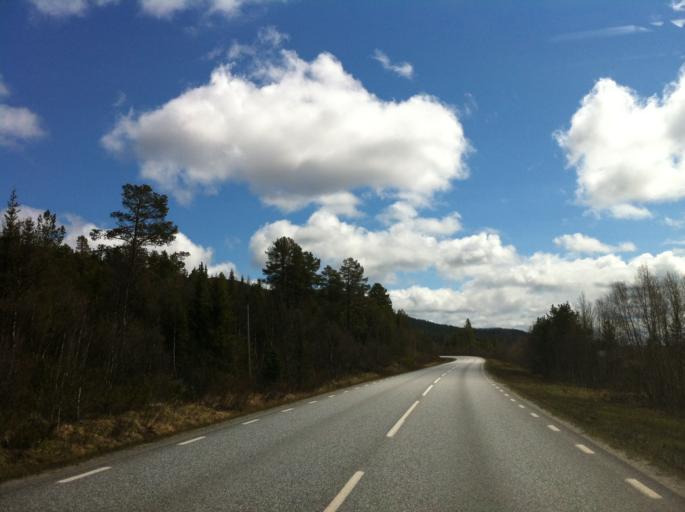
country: SE
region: Jaemtland
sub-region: Are Kommun
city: Are
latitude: 62.5985
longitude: 12.5298
